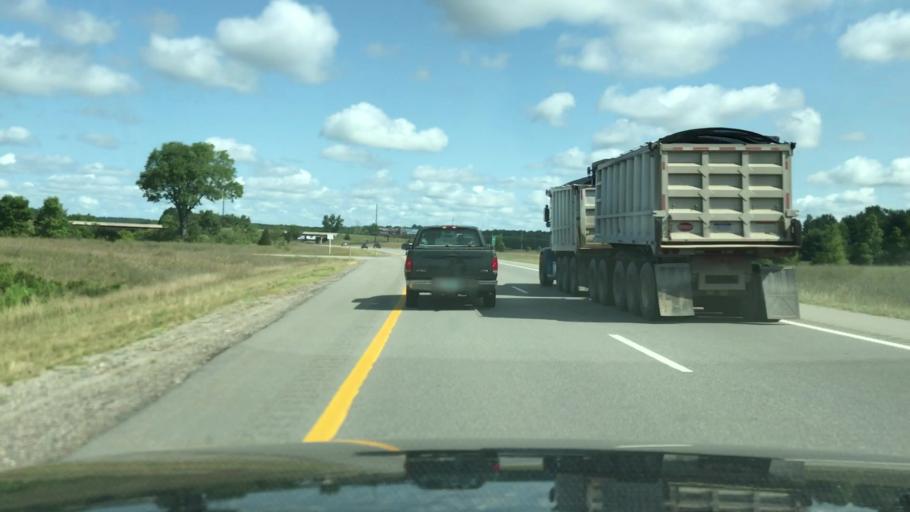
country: US
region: Michigan
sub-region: Mecosta County
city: Big Rapids
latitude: 43.5931
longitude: -85.4874
